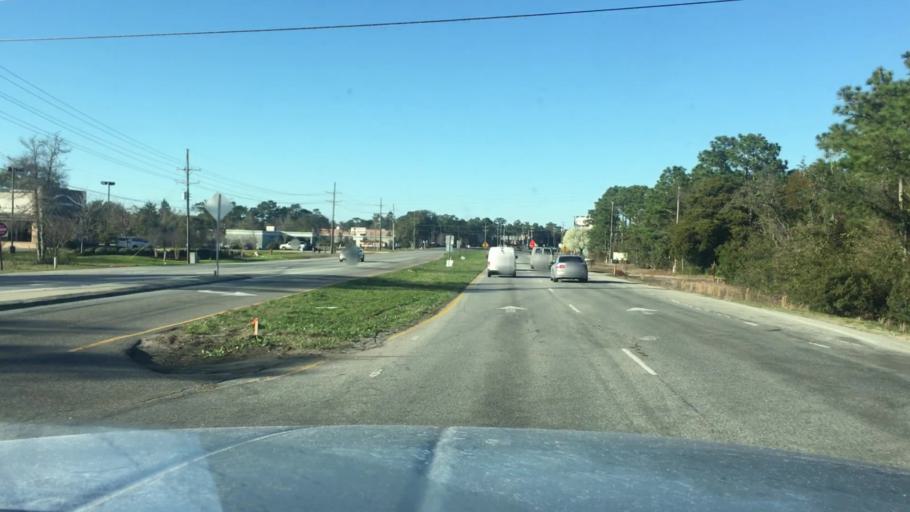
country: US
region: North Carolina
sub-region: New Hanover County
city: Myrtle Grove
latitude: 34.1218
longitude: -77.9000
